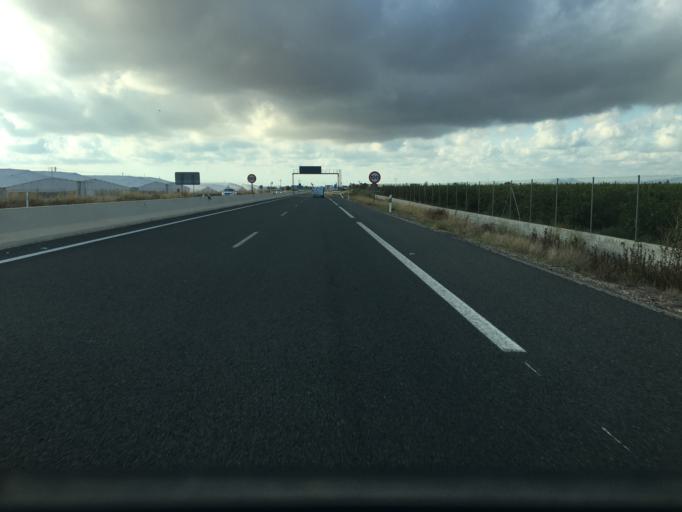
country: ES
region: Murcia
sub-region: Murcia
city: San Javier
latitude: 37.8259
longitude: -0.8542
